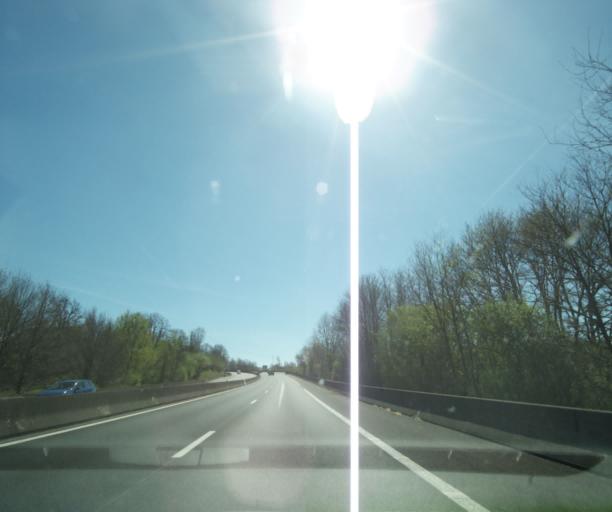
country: FR
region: Limousin
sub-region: Departement de la Haute-Vienne
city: Boisseuil
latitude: 45.7322
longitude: 1.3402
